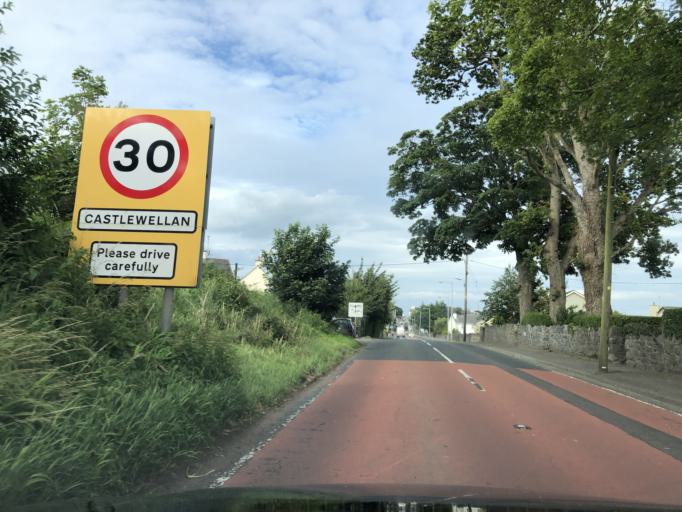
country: GB
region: Northern Ireland
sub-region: Down District
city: Castlewellan
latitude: 54.2544
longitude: -5.9526
